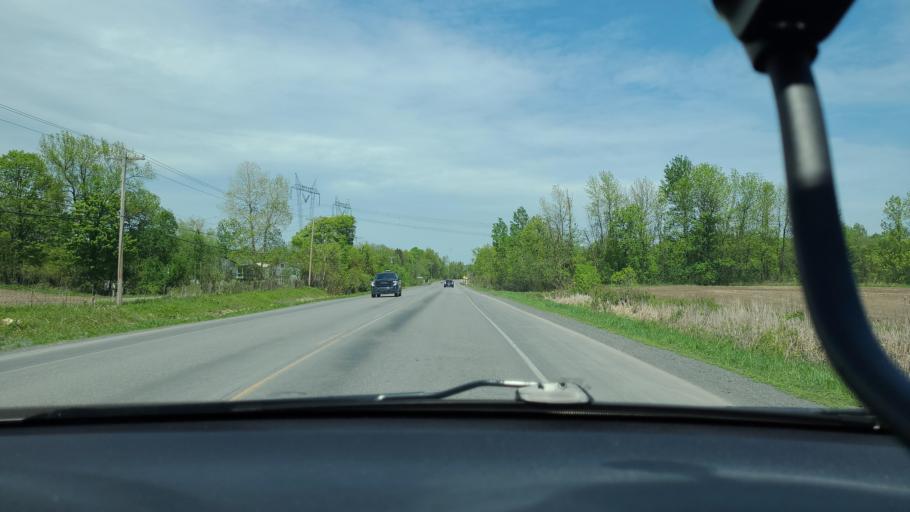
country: CA
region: Quebec
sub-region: Laurentides
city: Saint-Colomban
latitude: 45.6742
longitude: -74.2002
